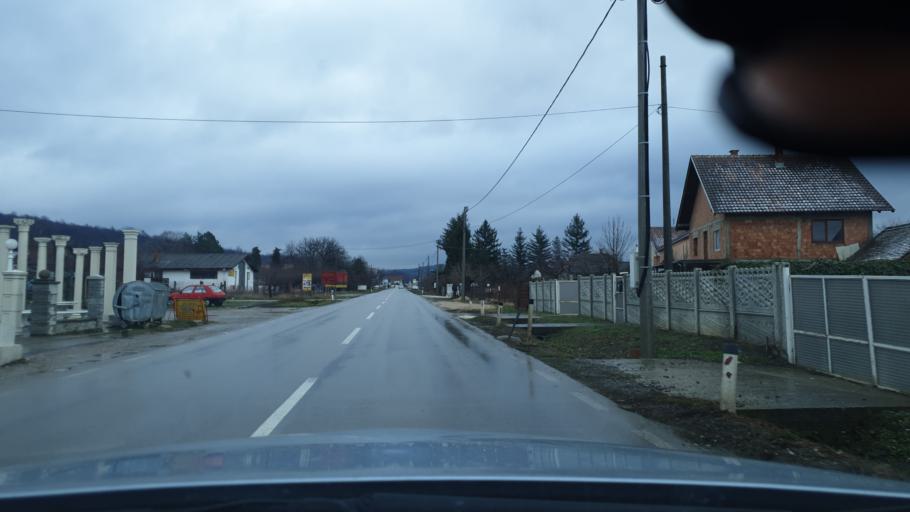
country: RS
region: Central Serbia
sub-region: Branicevski Okrug
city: Petrovac
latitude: 44.4059
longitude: 21.3937
